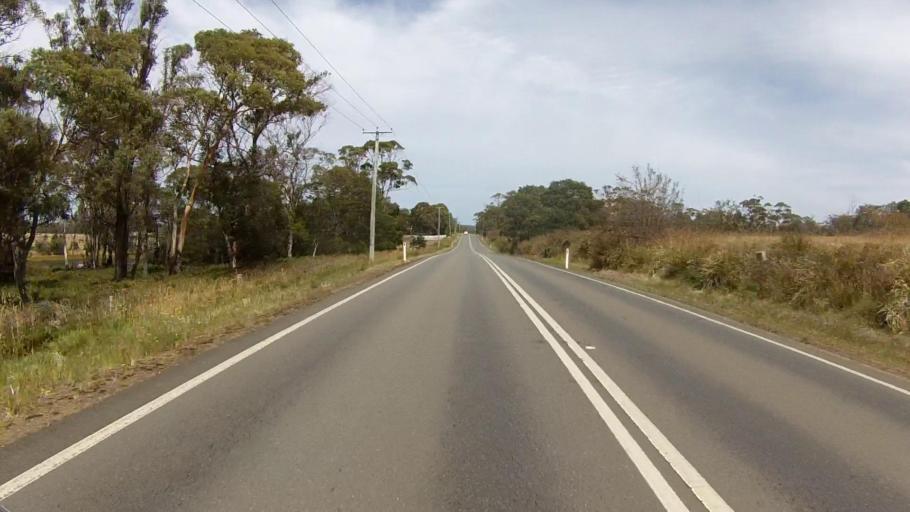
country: AU
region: Tasmania
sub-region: Clarence
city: Sandford
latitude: -43.0037
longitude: 147.4944
